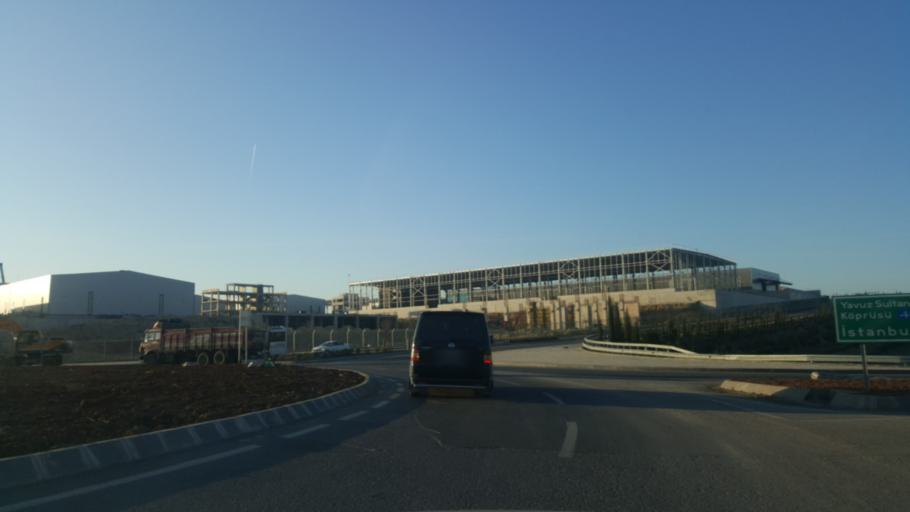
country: TR
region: Kocaeli
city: Tavsanli
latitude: 40.8276
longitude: 29.5612
